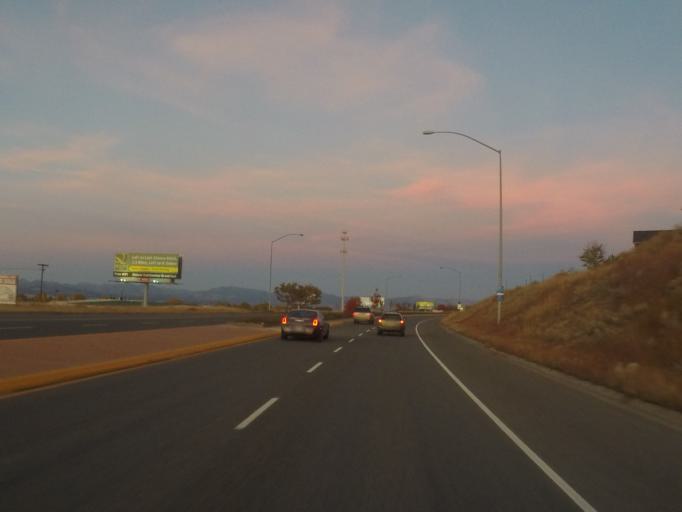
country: US
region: Montana
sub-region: Lewis and Clark County
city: Helena West Side
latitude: 46.6055
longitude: -112.0817
